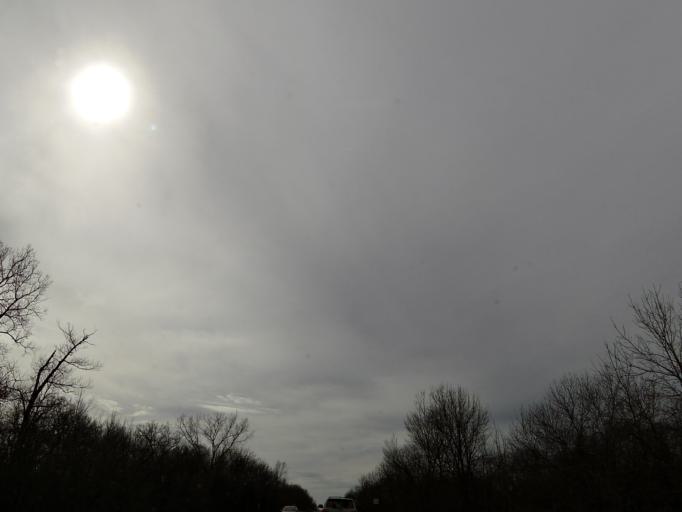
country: US
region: Minnesota
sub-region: Scott County
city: Prior Lake
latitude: 44.7294
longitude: -93.3953
